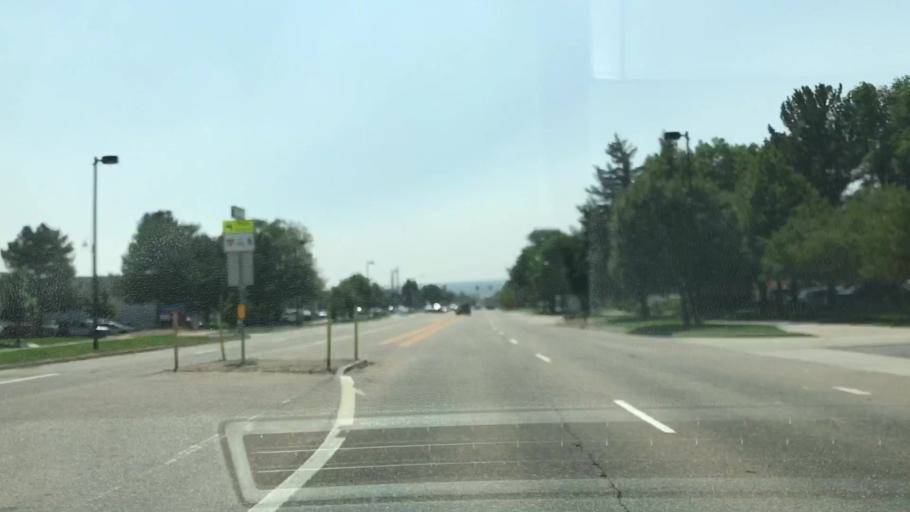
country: US
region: Colorado
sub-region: Boulder County
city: Boulder
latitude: 40.0349
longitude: -105.2585
